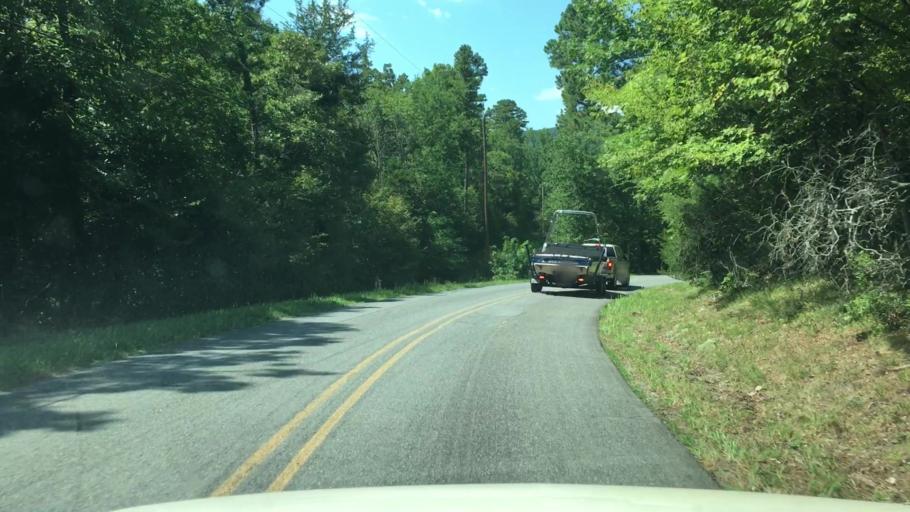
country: US
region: Arkansas
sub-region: Garland County
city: Piney
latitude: 34.5335
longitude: -93.3390
